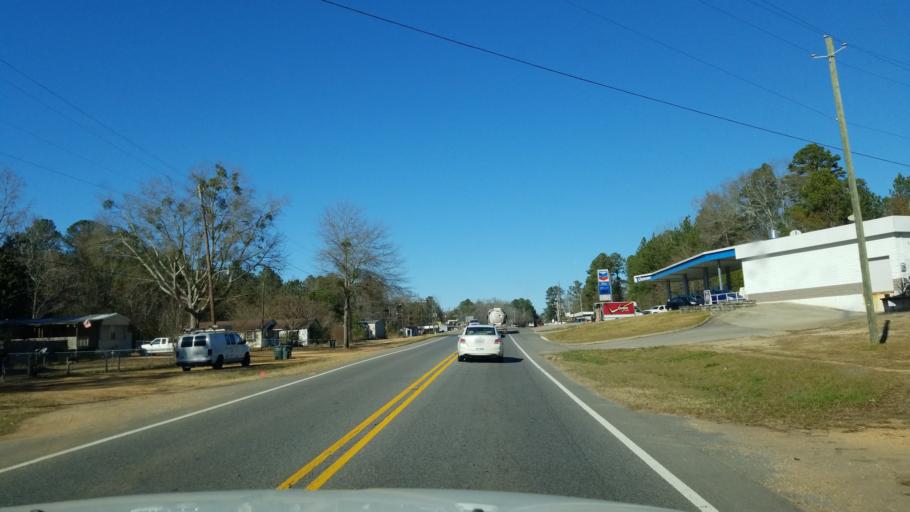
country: US
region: Alabama
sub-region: Pickens County
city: Gordo
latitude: 33.3242
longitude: -87.9104
